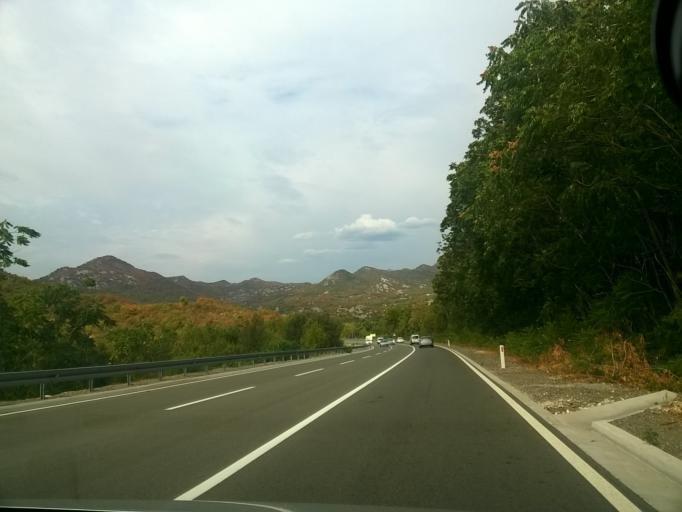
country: ME
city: Mojanovici
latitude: 42.3869
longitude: 19.0749
